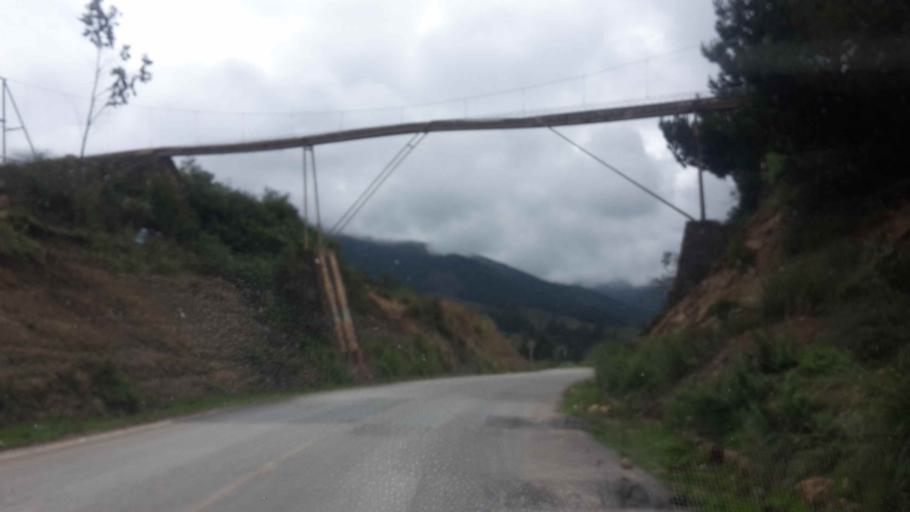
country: BO
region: Cochabamba
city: Totora
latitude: -17.5687
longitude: -65.3282
